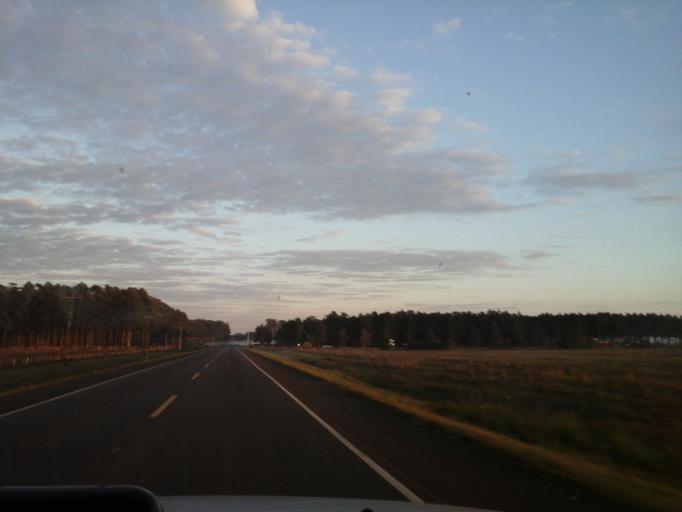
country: PY
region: Itapua
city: General Delgado
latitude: -27.0631
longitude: -56.6228
